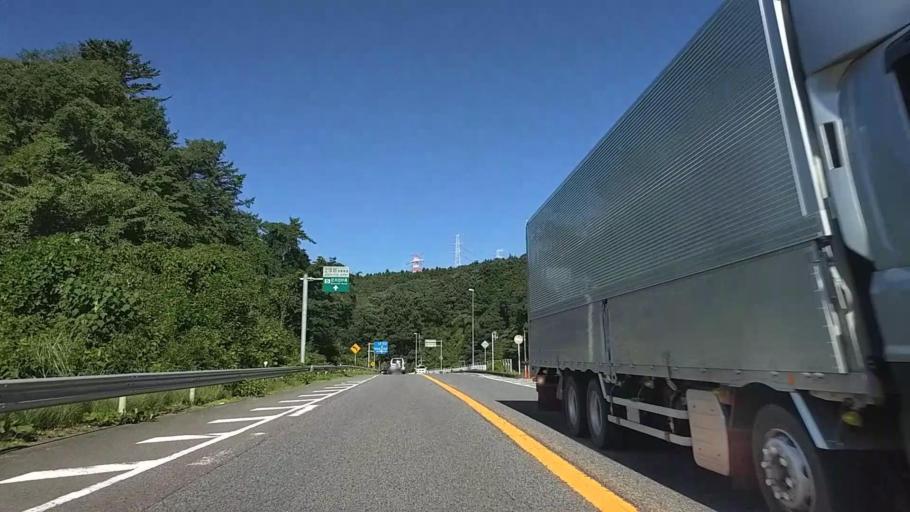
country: JP
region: Gunma
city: Annaka
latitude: 36.3203
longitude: 138.7908
